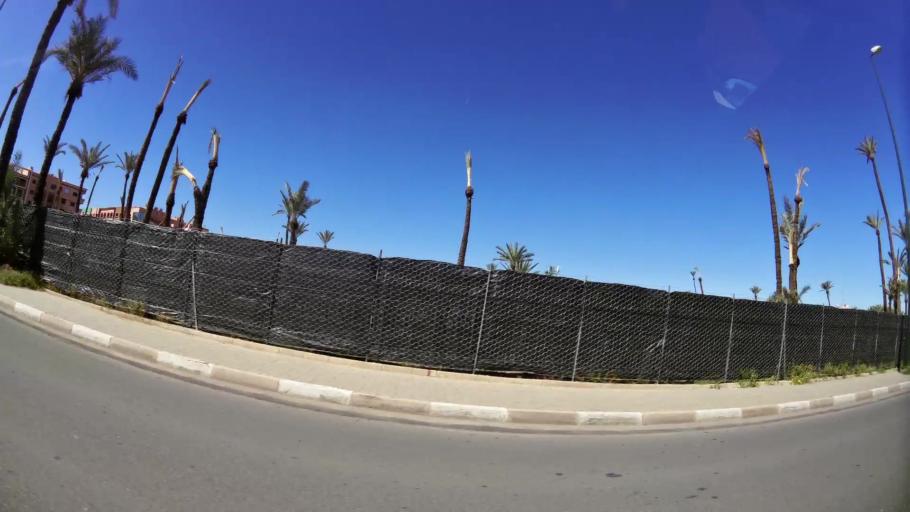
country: MA
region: Marrakech-Tensift-Al Haouz
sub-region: Marrakech
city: Marrakesh
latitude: 31.6405
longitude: -8.0103
